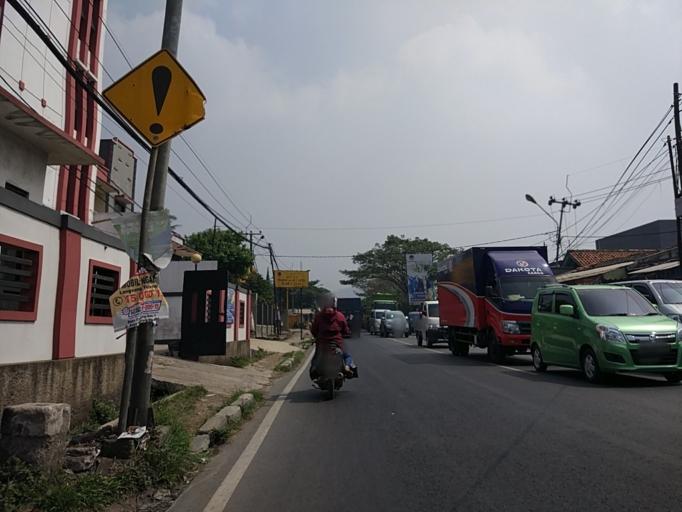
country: ID
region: West Java
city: Padalarang
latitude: -6.8355
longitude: 107.4703
